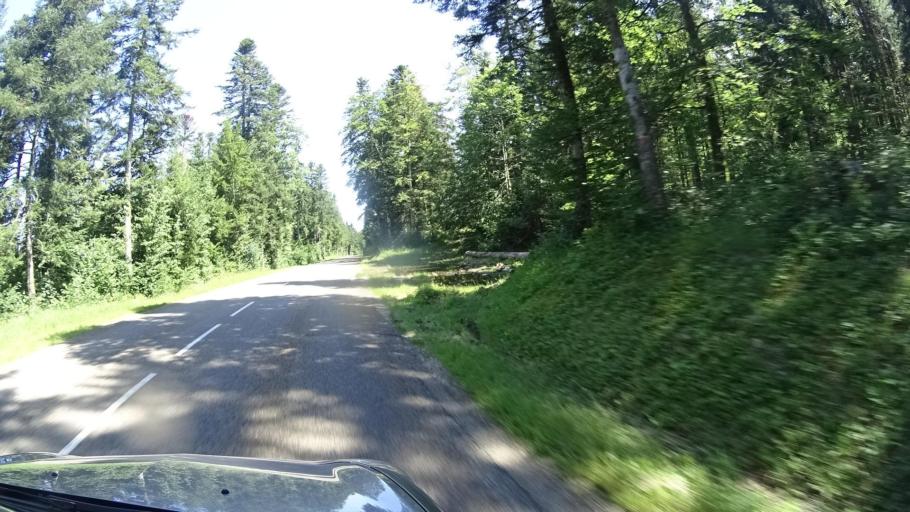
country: FR
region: Franche-Comte
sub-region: Departement du Jura
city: Longchaumois
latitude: 46.5109
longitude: 5.8944
